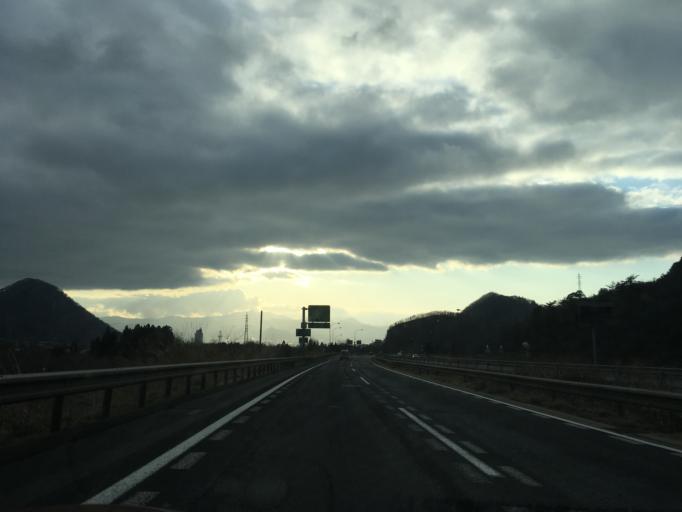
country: JP
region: Yamagata
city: Yamagata-shi
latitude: 38.2445
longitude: 140.3887
